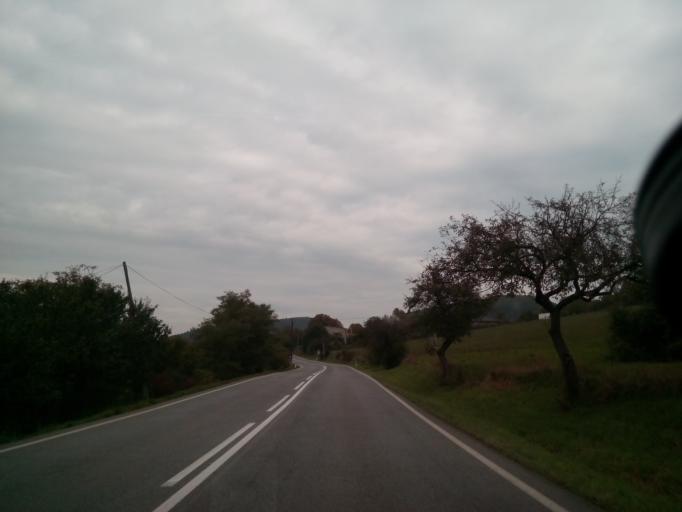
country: SK
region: Presovsky
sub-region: Okres Presov
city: Presov
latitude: 49.1025
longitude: 21.3152
